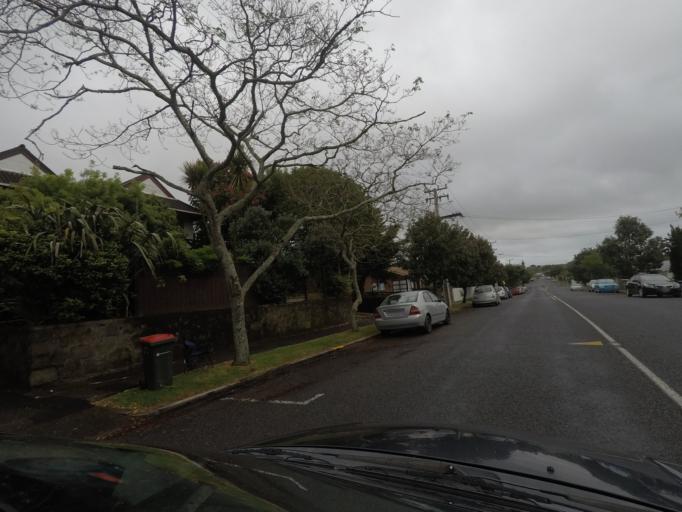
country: NZ
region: Auckland
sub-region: Auckland
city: Auckland
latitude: -36.8856
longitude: 174.7333
